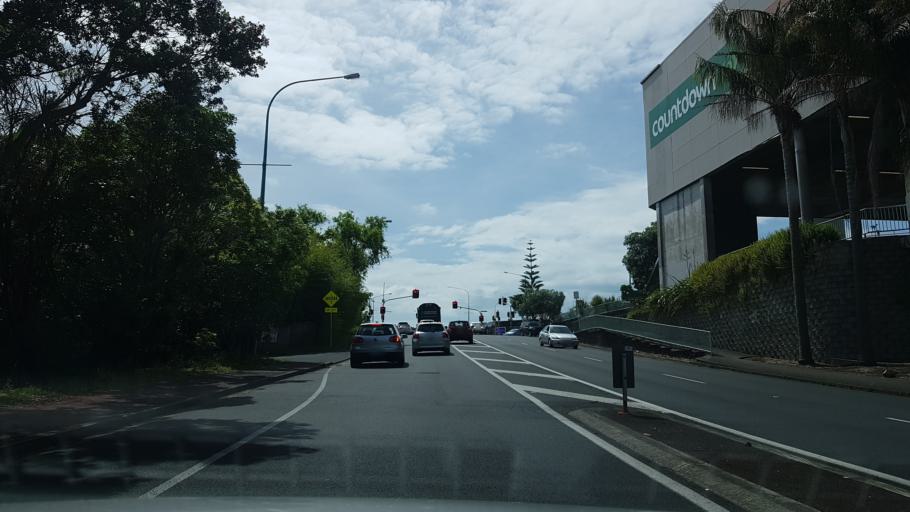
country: NZ
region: Auckland
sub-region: Auckland
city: North Shore
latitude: -36.8100
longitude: 174.7240
